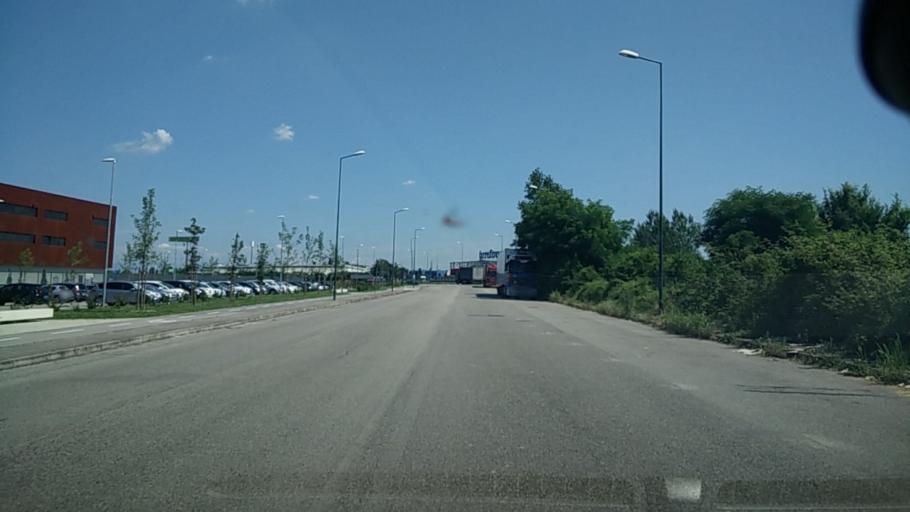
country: IT
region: Veneto
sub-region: Provincia di Venezia
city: Dese
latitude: 45.5418
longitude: 12.3009
